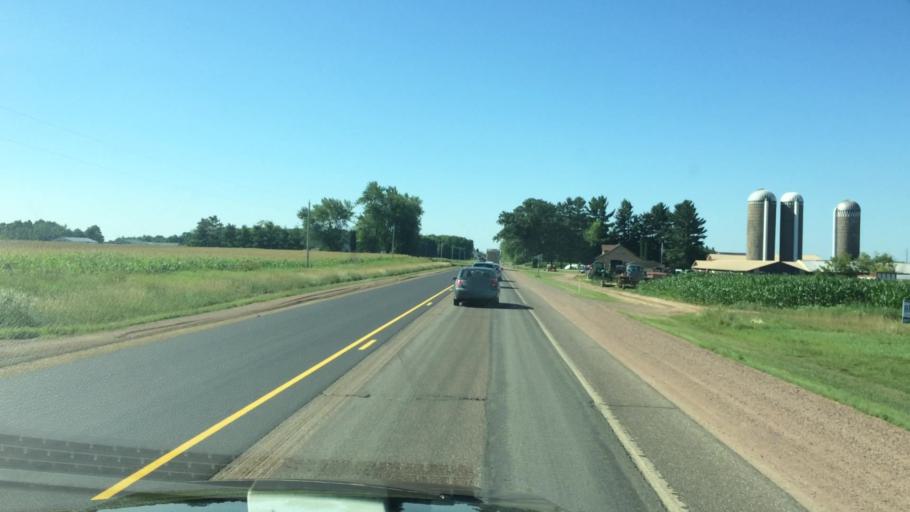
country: US
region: Wisconsin
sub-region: Marathon County
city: Stratford
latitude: 44.8652
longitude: -90.0791
